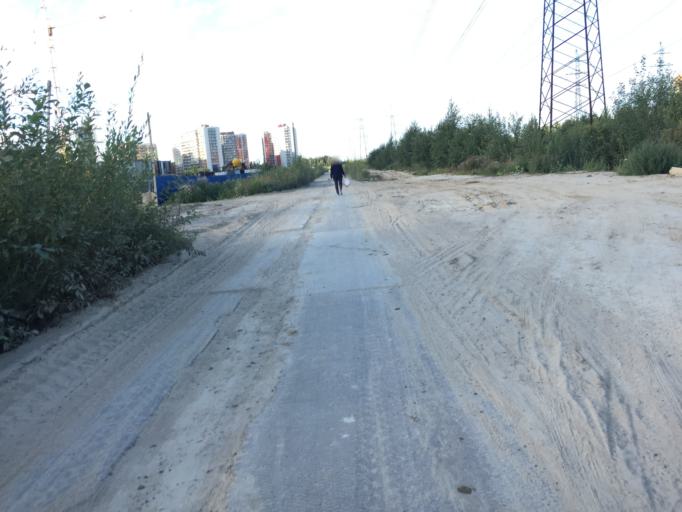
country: RU
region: Leningrad
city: Murino
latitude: 60.0636
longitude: 30.4473
